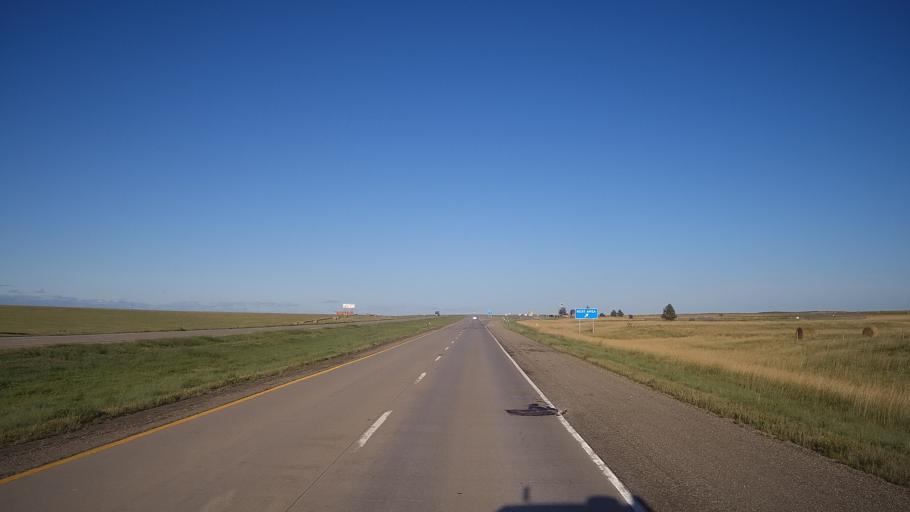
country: US
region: South Dakota
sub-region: Jackson County
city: Kadoka
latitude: 43.8426
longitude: -101.2401
